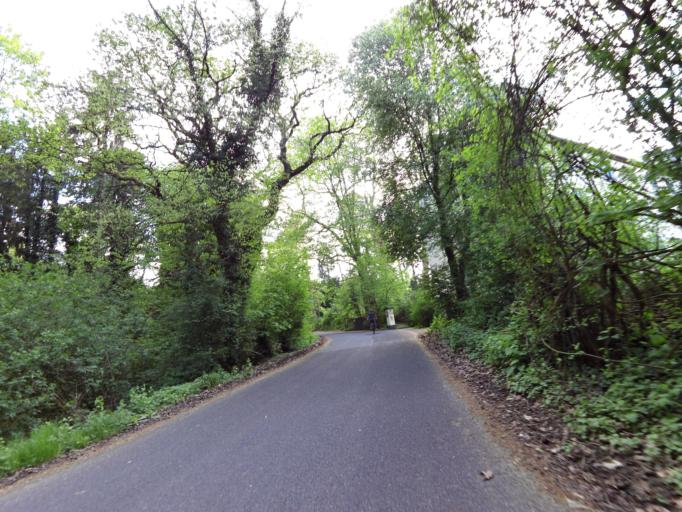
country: DE
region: North Rhine-Westphalia
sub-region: Regierungsbezirk Koln
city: Bonn
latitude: 50.6908
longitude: 7.1145
